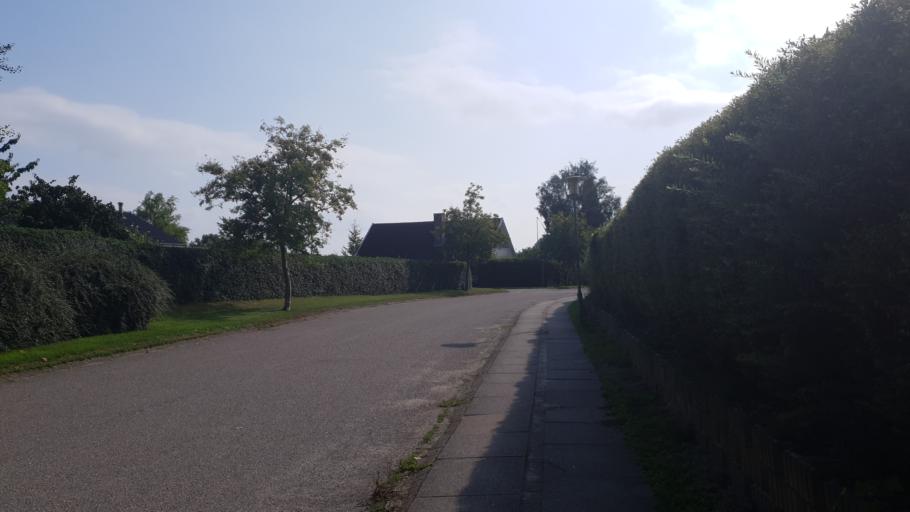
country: DK
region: South Denmark
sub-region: Fredericia Kommune
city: Snoghoj
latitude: 55.5489
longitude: 9.7087
